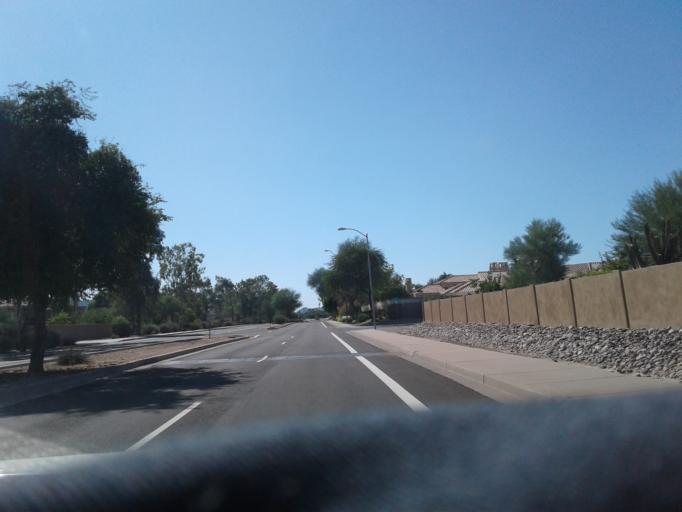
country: US
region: Arizona
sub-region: Maricopa County
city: Paradise Valley
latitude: 33.5750
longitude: -111.9207
